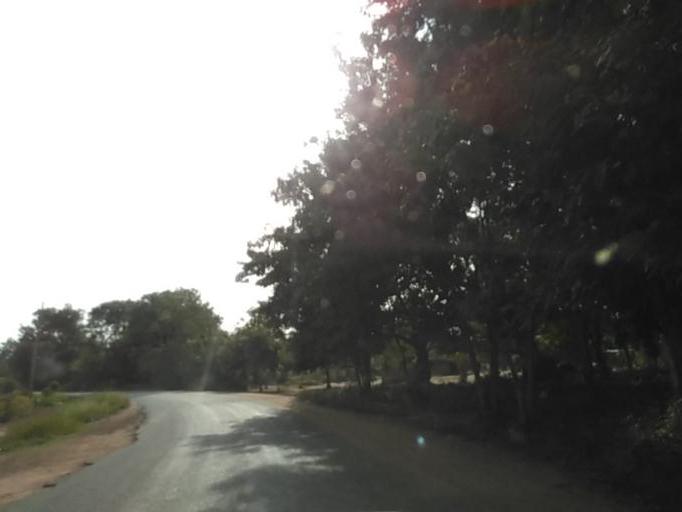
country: GH
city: Akropong
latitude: 6.1015
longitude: 0.1537
